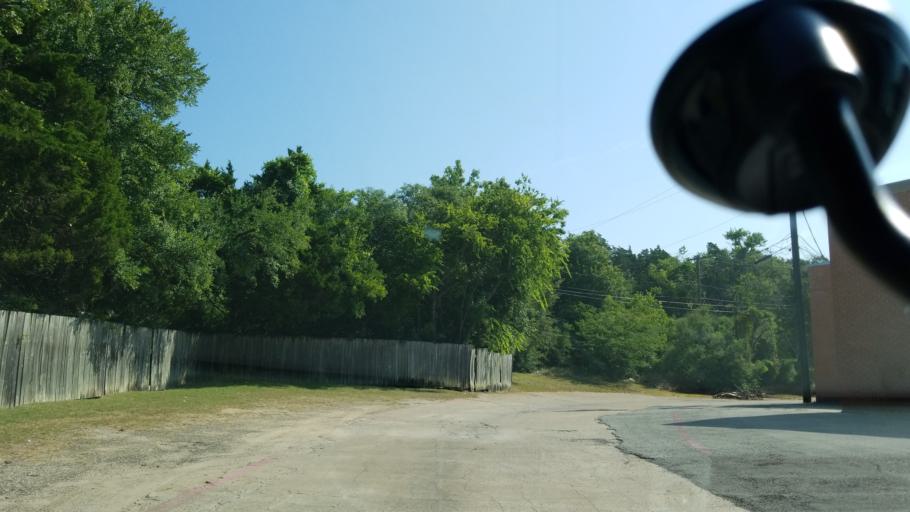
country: US
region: Texas
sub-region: Dallas County
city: Cockrell Hill
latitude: 32.7063
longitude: -96.8586
